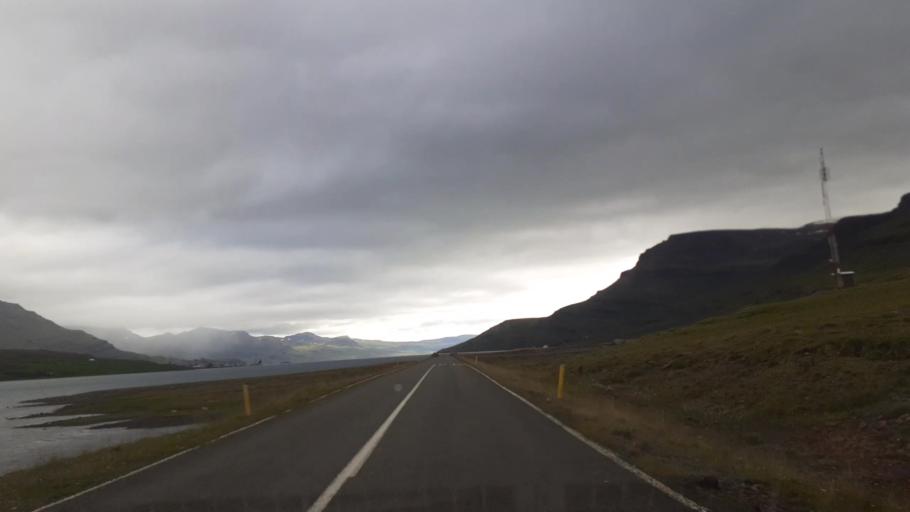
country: IS
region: East
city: Reydarfjoerdur
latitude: 65.0170
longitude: -14.2107
